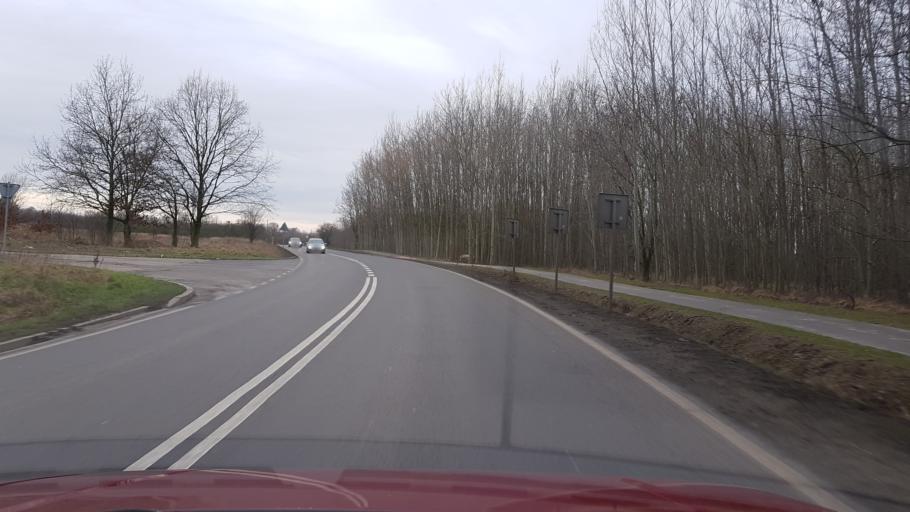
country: PL
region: West Pomeranian Voivodeship
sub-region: Powiat policki
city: Police
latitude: 53.5857
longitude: 14.5511
